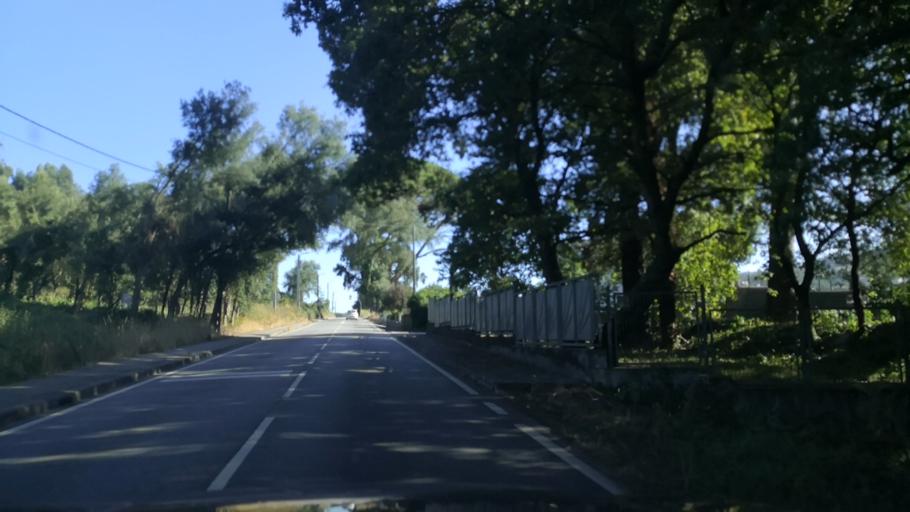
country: PT
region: Porto
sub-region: Santo Tirso
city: Sao Miguel do Couto
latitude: 41.3071
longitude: -8.4709
